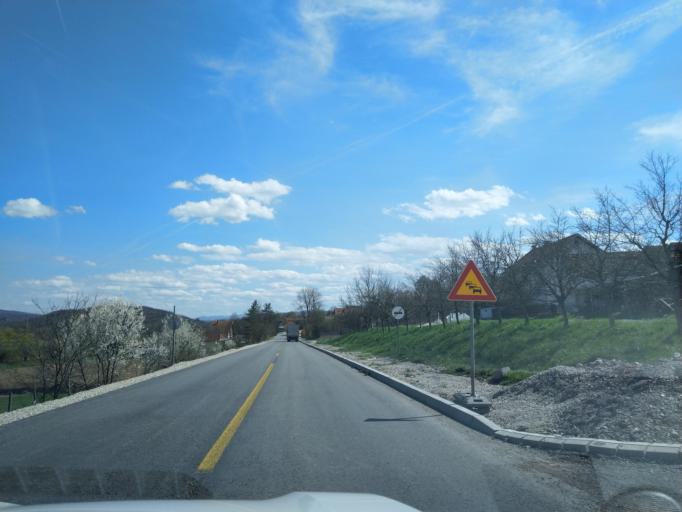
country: RS
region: Central Serbia
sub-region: Zlatiborski Okrug
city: Pozega
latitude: 43.8271
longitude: 20.0780
